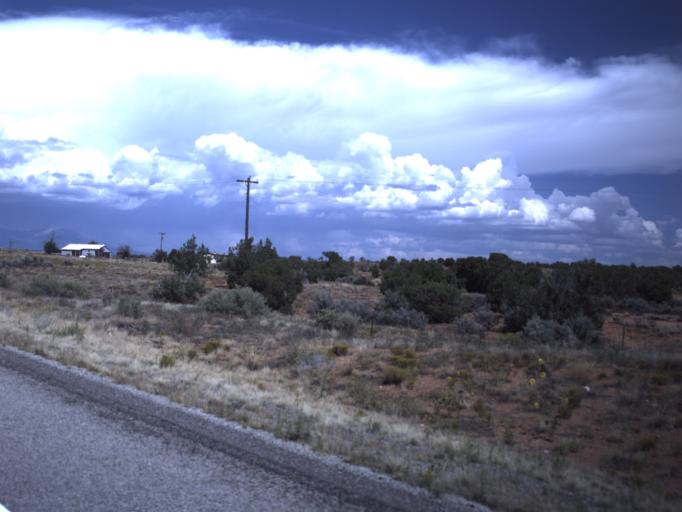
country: US
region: Utah
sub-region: San Juan County
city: Blanding
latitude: 37.4777
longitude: -109.4679
